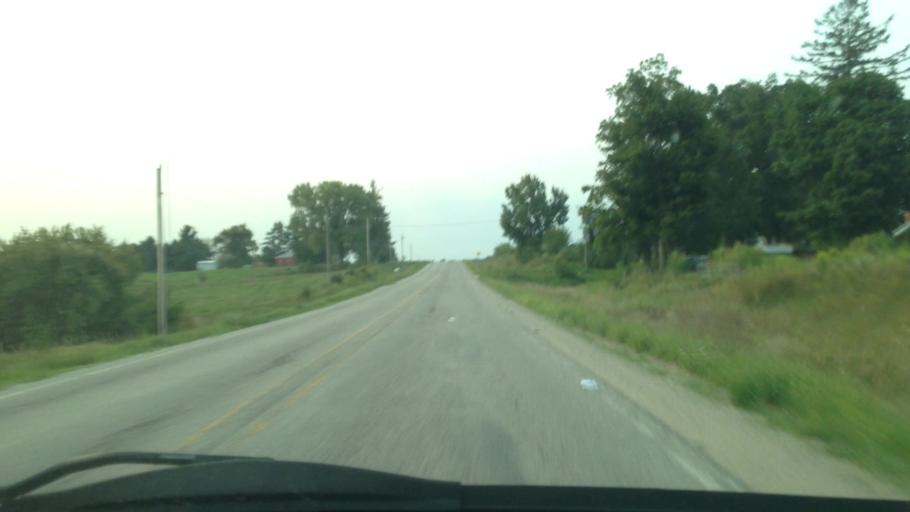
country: US
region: Iowa
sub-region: Benton County
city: Urbana
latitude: 42.1450
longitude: -91.8789
